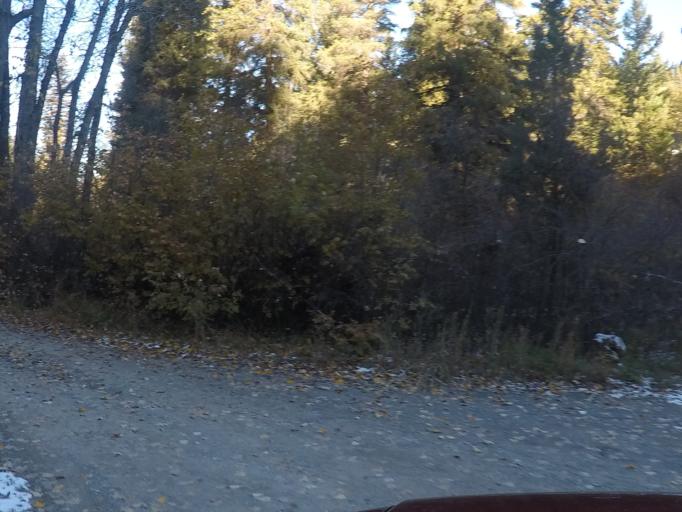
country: US
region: Montana
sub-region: Broadwater County
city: Townsend
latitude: 46.3255
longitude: -111.1927
